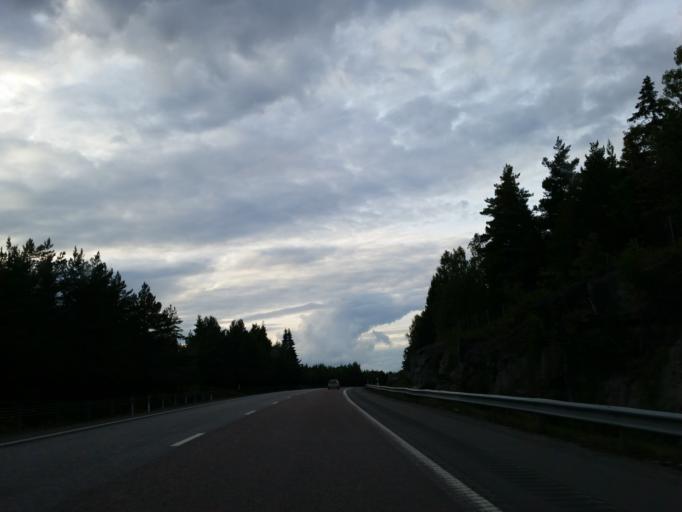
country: SE
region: Uppsala
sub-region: Knivsta Kommun
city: Knivsta
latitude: 59.7623
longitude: 17.7960
